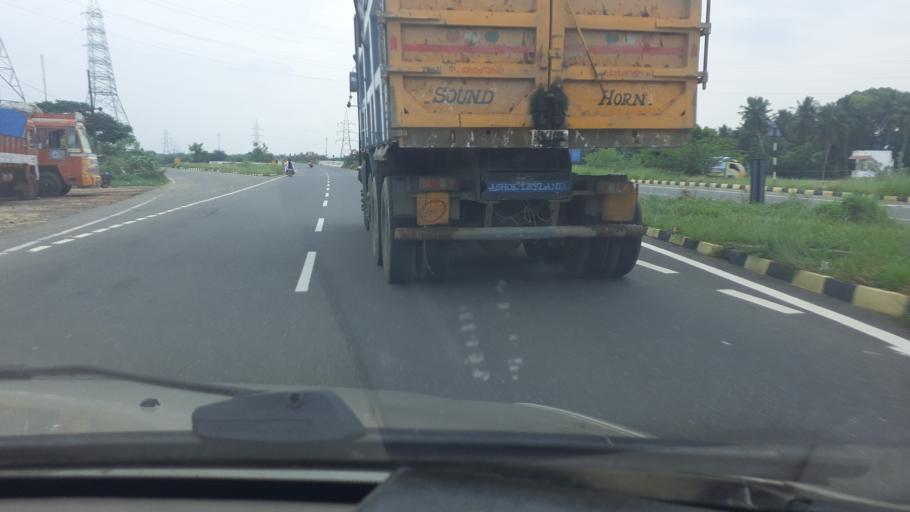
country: IN
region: Tamil Nadu
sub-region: Madurai
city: Tirupparangunram
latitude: 9.8295
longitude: 77.9753
